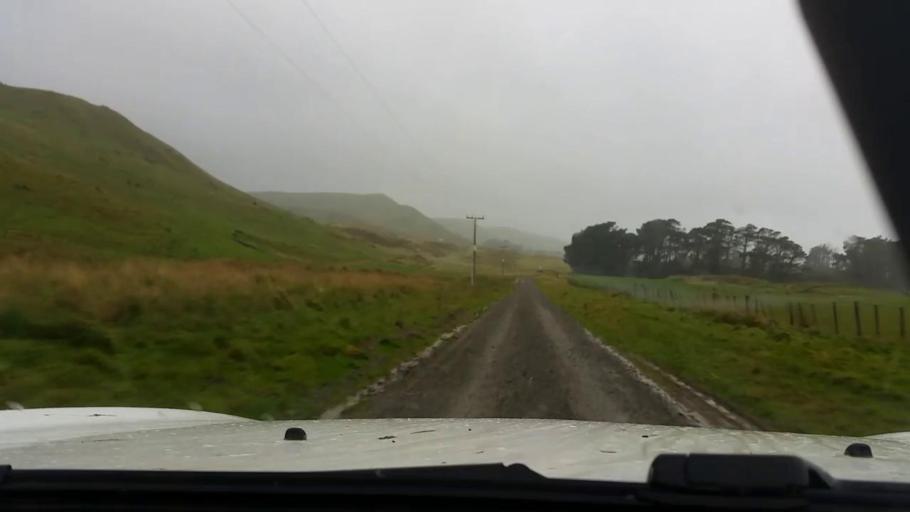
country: NZ
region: Wellington
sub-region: Masterton District
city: Masterton
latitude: -41.2546
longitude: 175.9095
